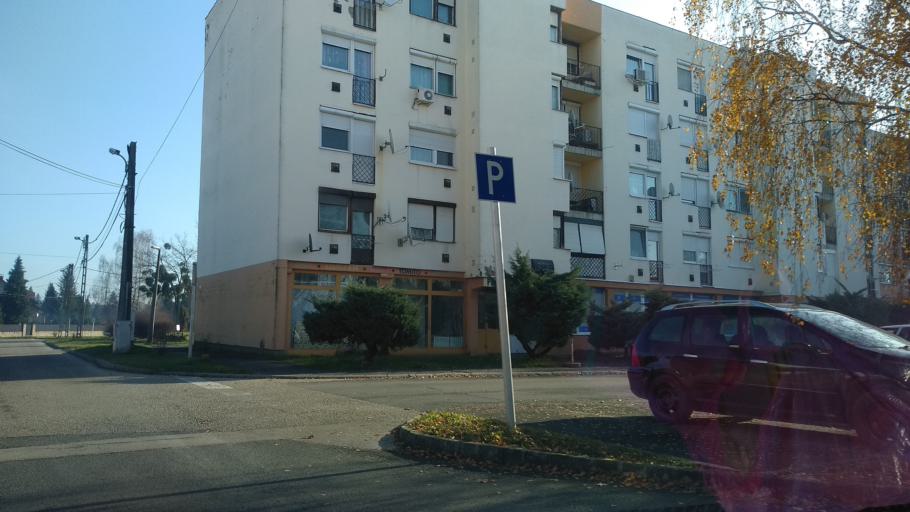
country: HU
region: Somogy
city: Barcs
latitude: 45.9612
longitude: 17.4667
